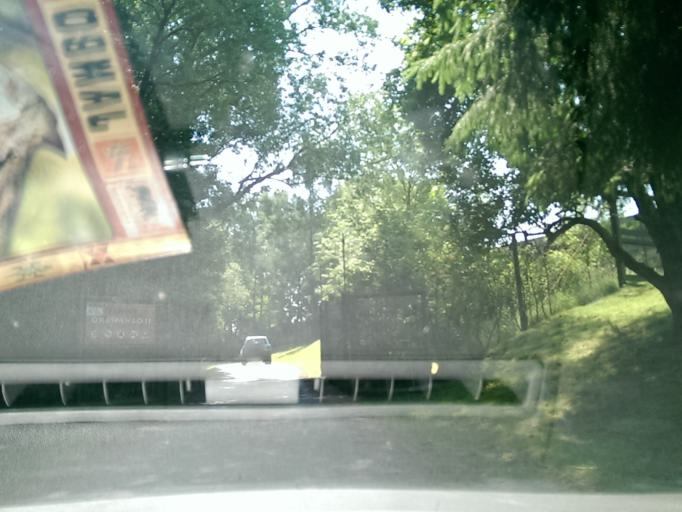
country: CZ
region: Kralovehradecky
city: Dvur Kralove nad Labem
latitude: 50.4321
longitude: 15.7842
